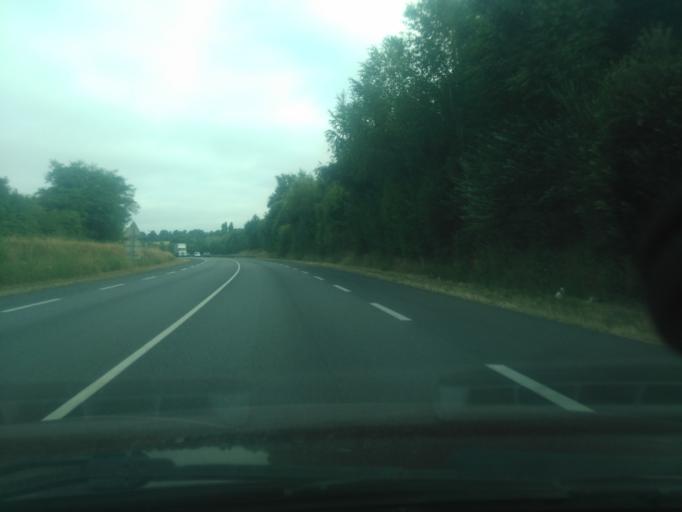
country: FR
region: Pays de la Loire
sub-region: Departement de la Vendee
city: La Roche-sur-Yon
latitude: 46.6884
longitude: -1.4129
